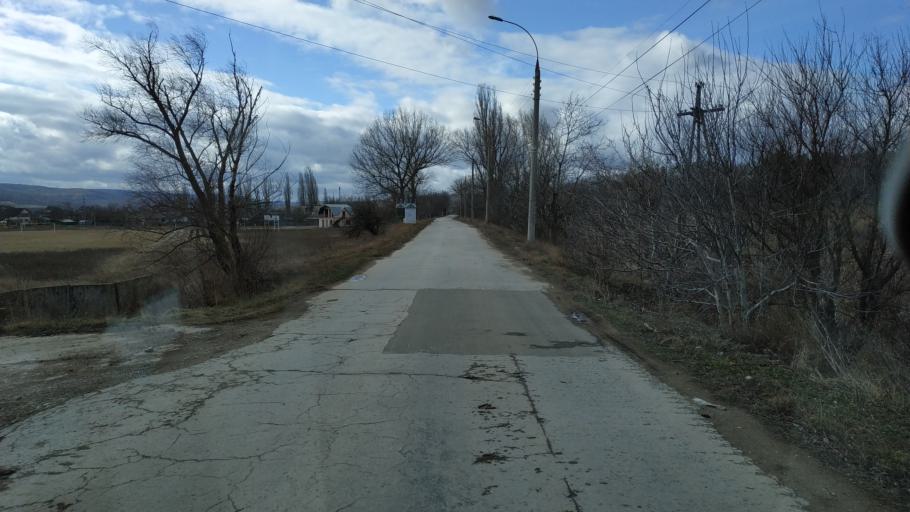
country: MD
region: Stinga Nistrului
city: Bucovat
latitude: 47.1895
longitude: 28.4774
